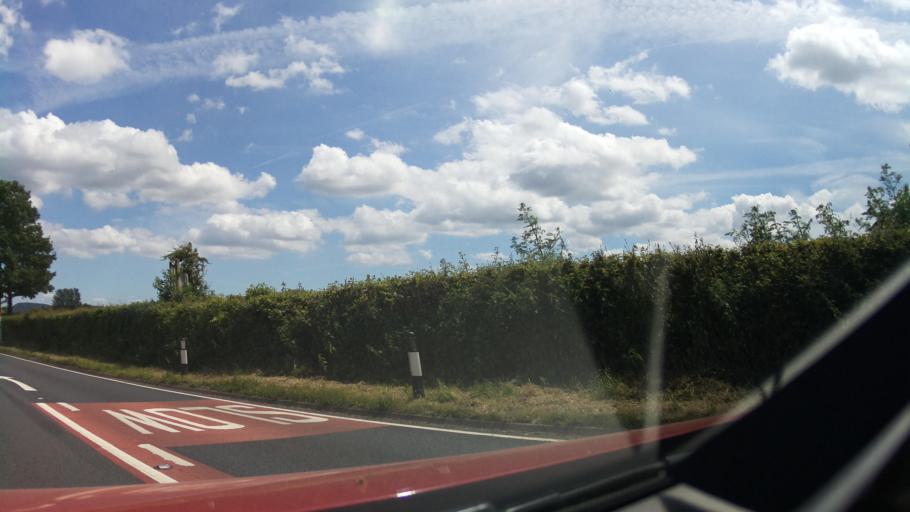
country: GB
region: England
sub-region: Herefordshire
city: Sellack
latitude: 51.9213
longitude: -2.6459
